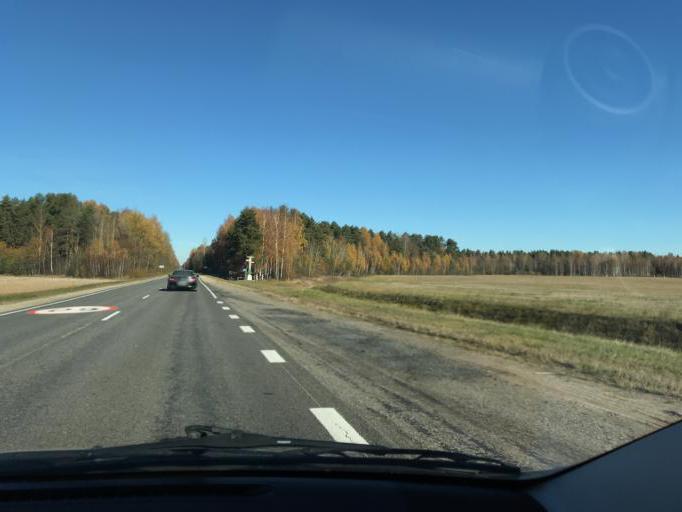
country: BY
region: Vitebsk
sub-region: Ushatski Rayon
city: Ushachy
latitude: 55.0587
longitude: 28.7523
